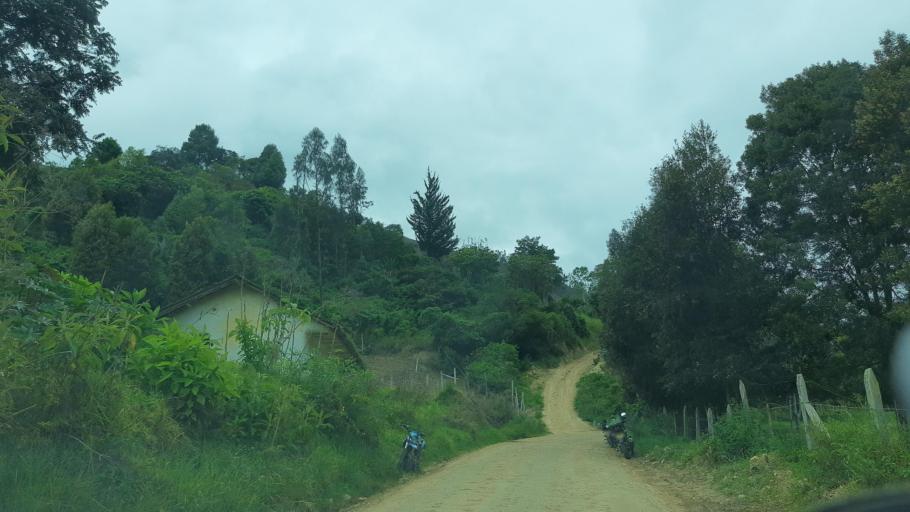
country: CO
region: Boyaca
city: Tibana
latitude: 5.3182
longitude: -73.4395
